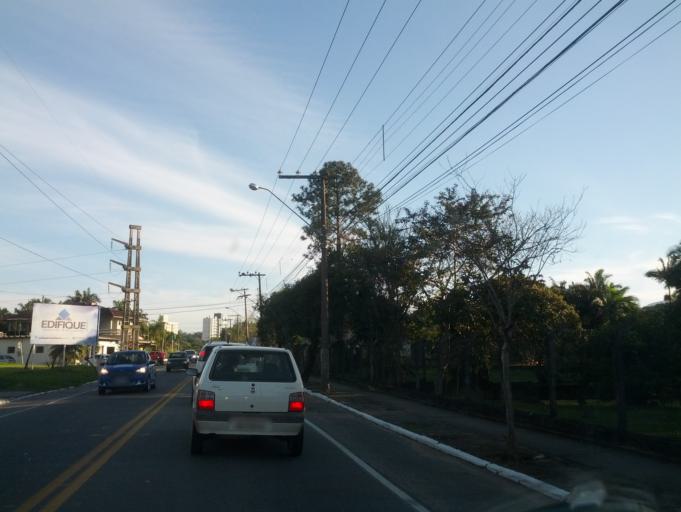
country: BR
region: Santa Catarina
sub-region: Indaial
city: Indaial
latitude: -26.8900
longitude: -49.2250
